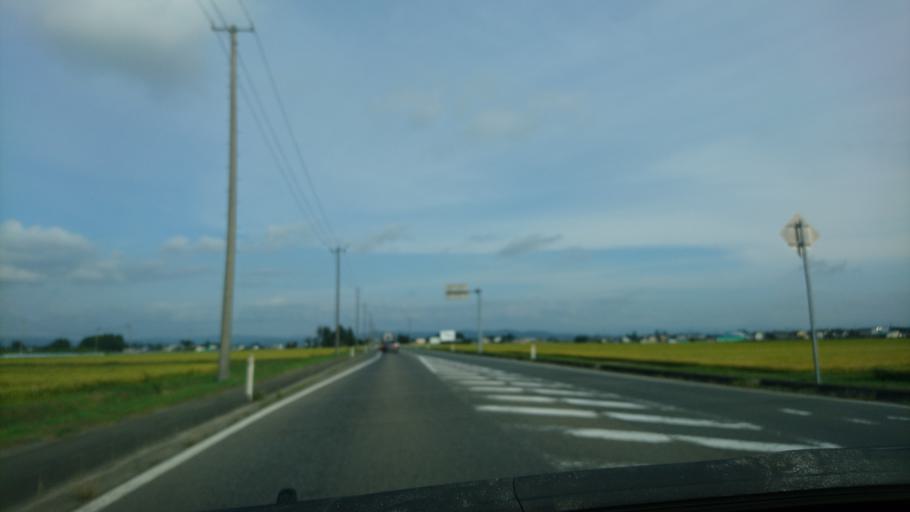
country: JP
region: Iwate
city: Kitakami
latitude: 39.3031
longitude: 141.0443
